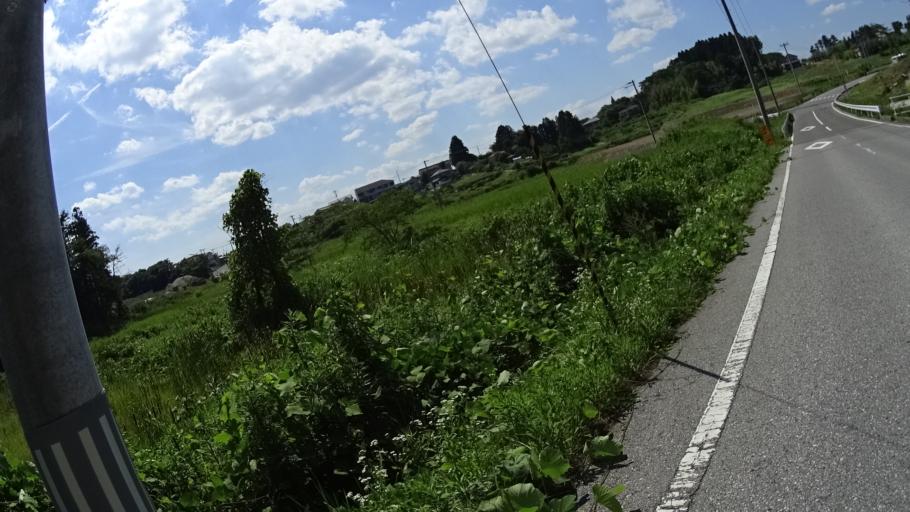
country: JP
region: Iwate
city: Ofunato
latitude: 38.8497
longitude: 141.6229
